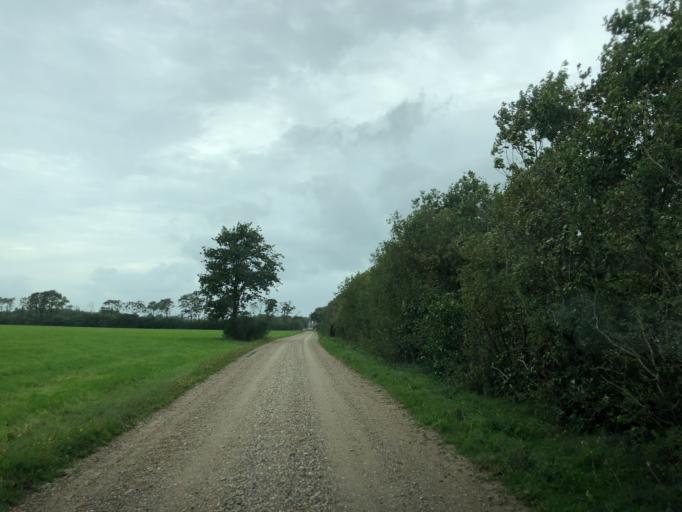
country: DK
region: Central Jutland
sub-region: Holstebro Kommune
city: Holstebro
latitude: 56.2368
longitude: 8.5242
